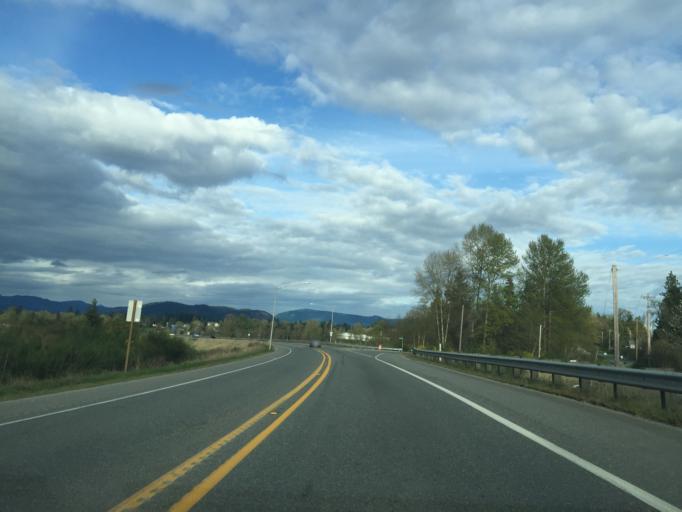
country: US
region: Washington
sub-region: Snohomish County
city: Arlington
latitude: 48.1883
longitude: -122.1452
